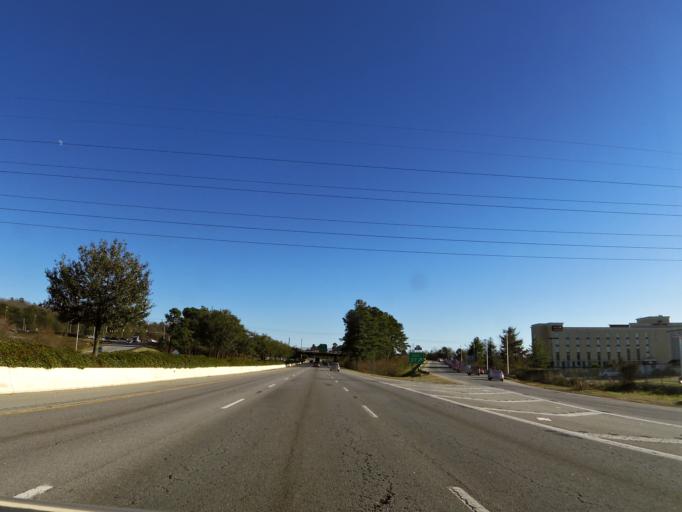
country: US
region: South Carolina
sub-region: Greenville County
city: Mauldin
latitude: 34.8416
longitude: -82.3167
